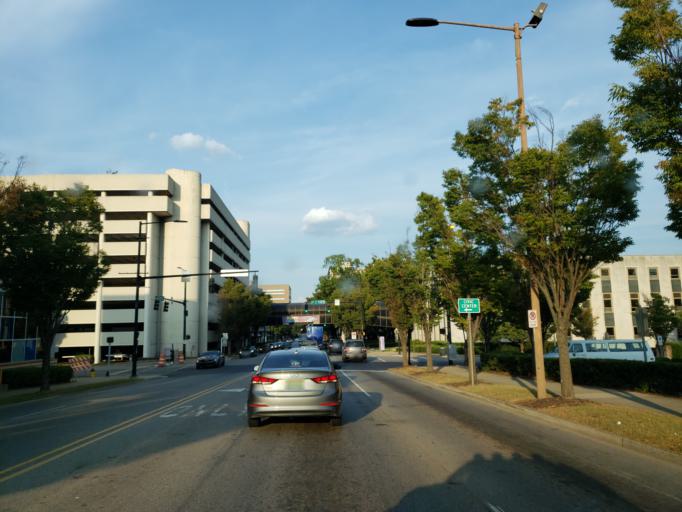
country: US
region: Alabama
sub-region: Jefferson County
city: Birmingham
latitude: 33.5206
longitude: -86.8124
